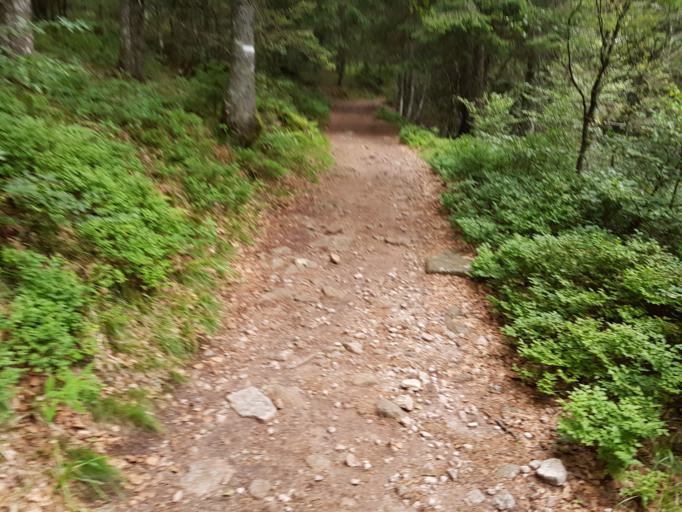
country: FR
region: Alsace
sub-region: Departement du Haut-Rhin
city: Soultzeren
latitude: 48.0889
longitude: 7.0599
